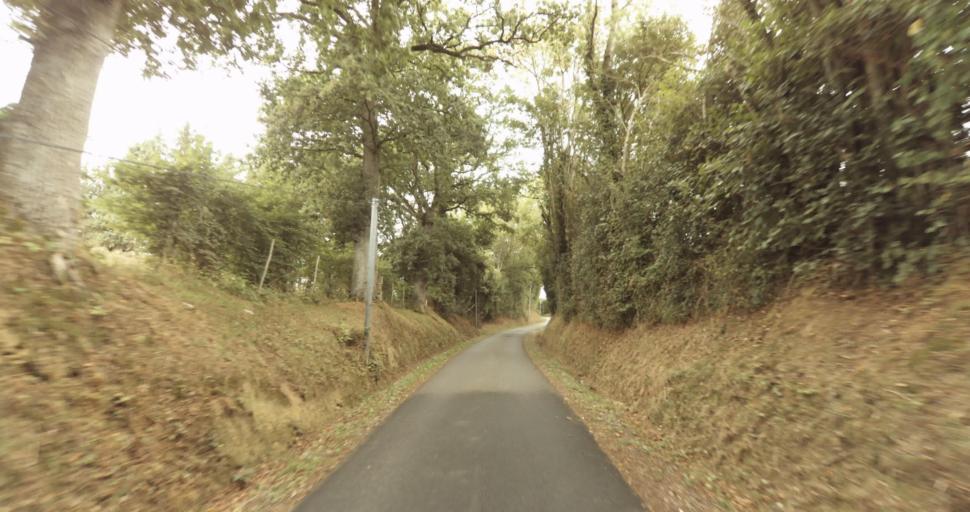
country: FR
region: Lower Normandy
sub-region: Departement de l'Orne
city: Sees
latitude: 48.6738
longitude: 0.2619
